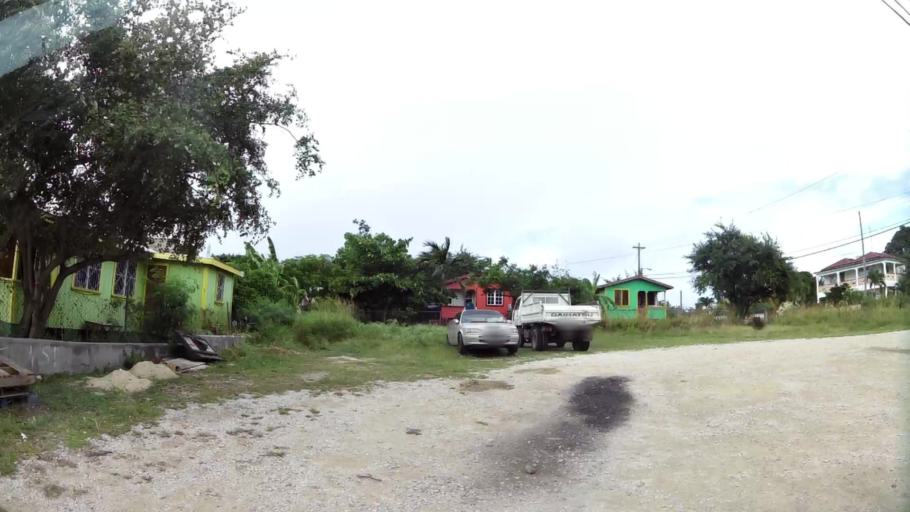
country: AG
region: Saint John
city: Potters Village
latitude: 17.0936
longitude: -61.8140
